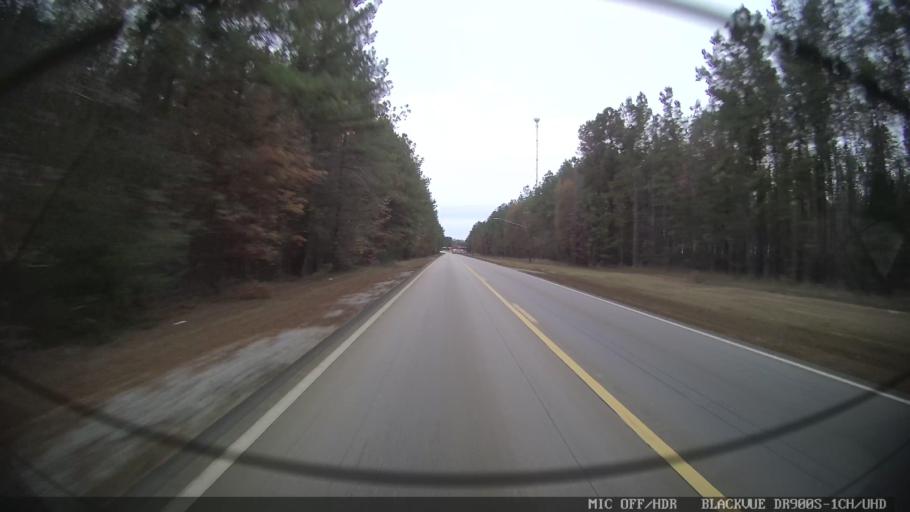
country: US
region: Mississippi
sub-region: Clarke County
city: Stonewall
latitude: 32.0536
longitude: -88.8980
